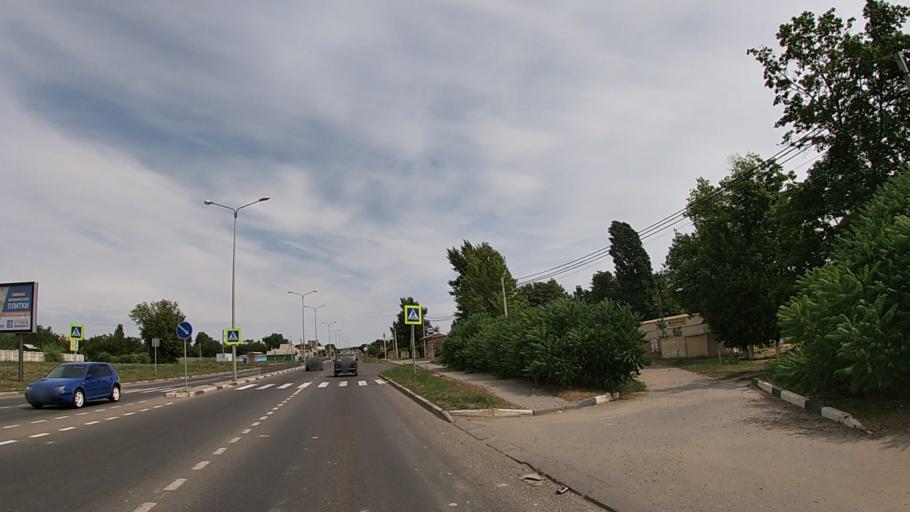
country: RU
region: Belgorod
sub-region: Belgorodskiy Rayon
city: Belgorod
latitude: 50.6187
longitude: 36.5397
